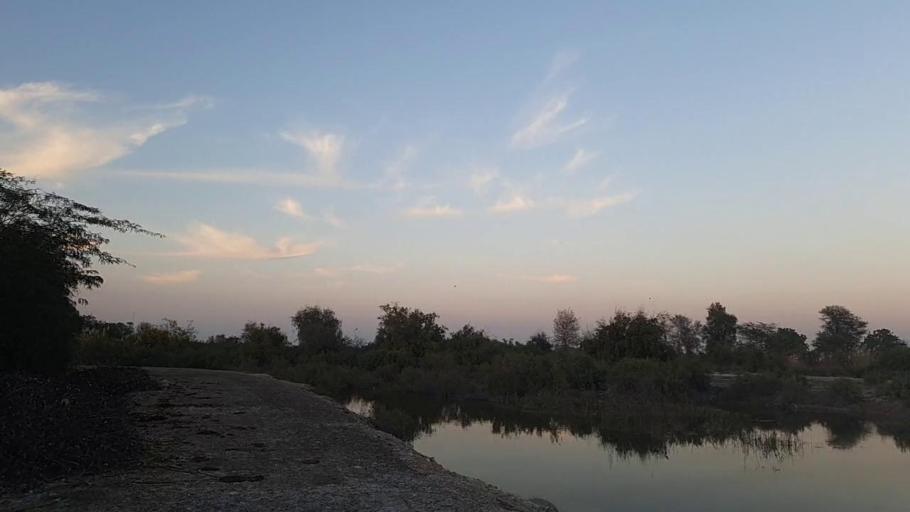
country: PK
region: Sindh
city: Bandhi
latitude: 26.5989
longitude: 68.3373
